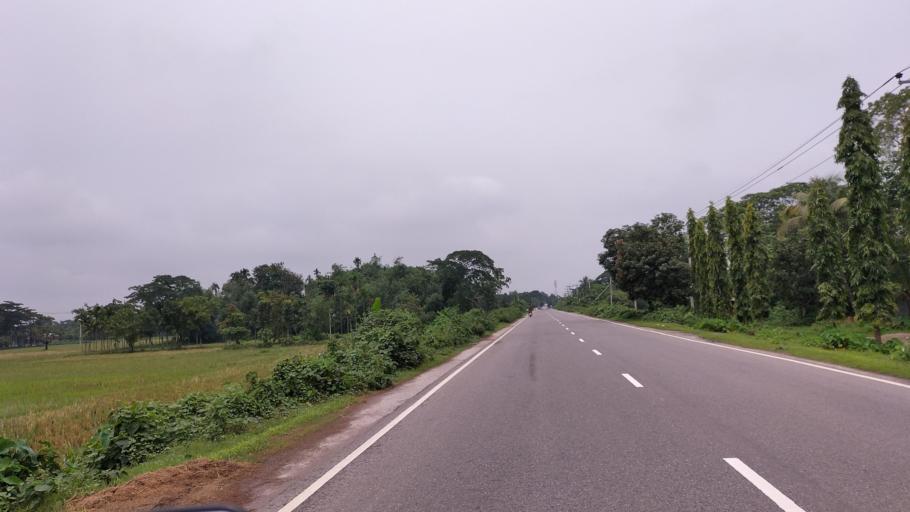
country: BD
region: Dhaka
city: Netrakona
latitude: 24.8507
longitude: 90.6328
